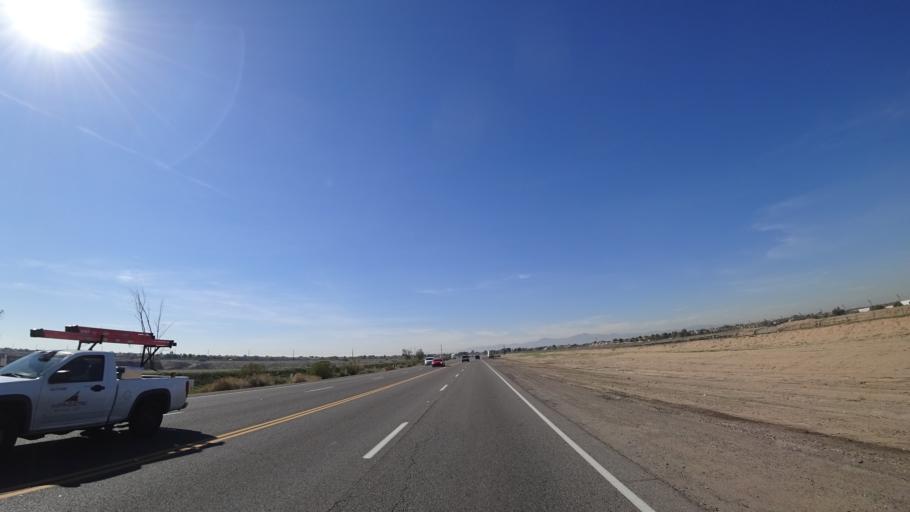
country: US
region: Arizona
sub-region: Maricopa County
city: Litchfield Park
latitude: 33.5076
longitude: -112.3184
